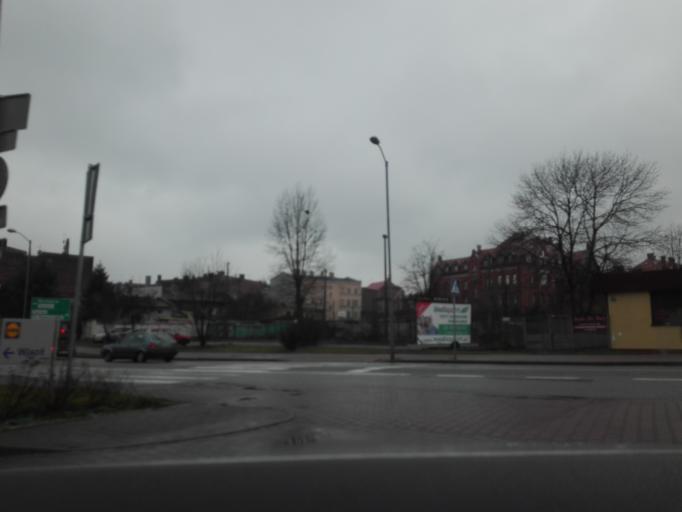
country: PL
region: Silesian Voivodeship
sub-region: Katowice
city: Katowice
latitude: 50.2590
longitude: 19.0360
